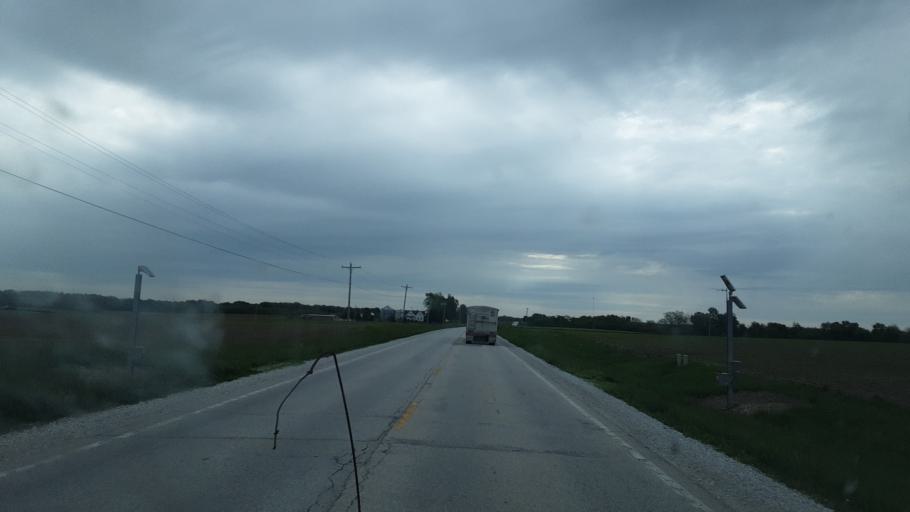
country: US
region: Illinois
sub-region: Fulton County
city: Lewistown
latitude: 40.3422
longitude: -90.2418
